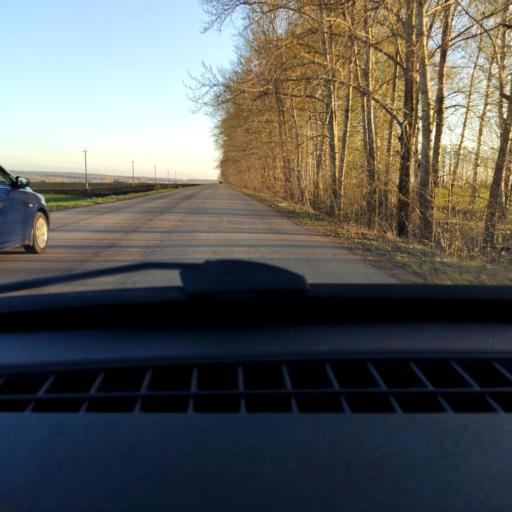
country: RU
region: Bashkortostan
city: Avdon
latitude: 54.5132
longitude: 55.6267
